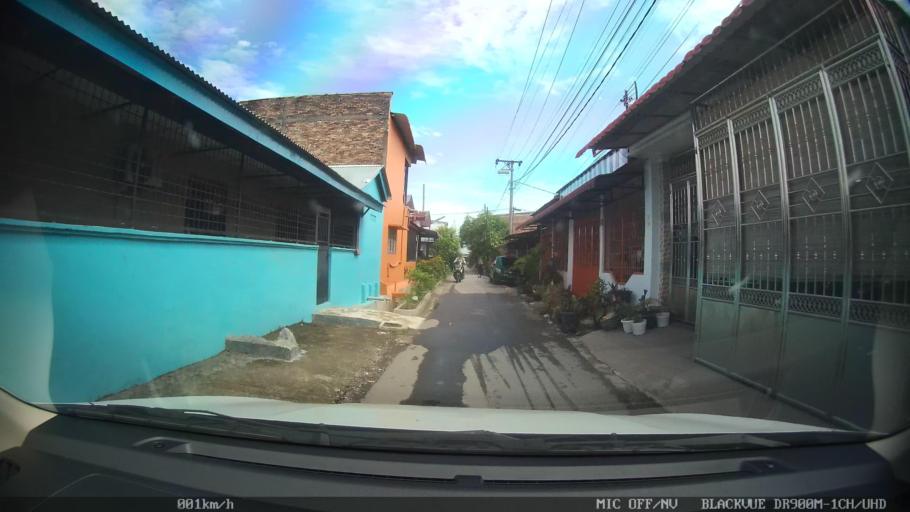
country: ID
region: North Sumatra
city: Medan
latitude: 3.5908
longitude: 98.7392
